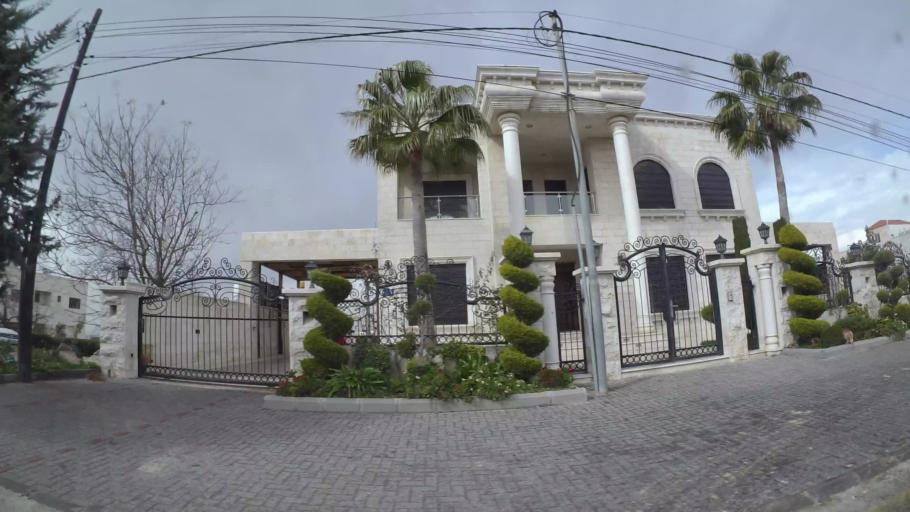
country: JO
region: Amman
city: Wadi as Sir
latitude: 31.9809
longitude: 35.8219
